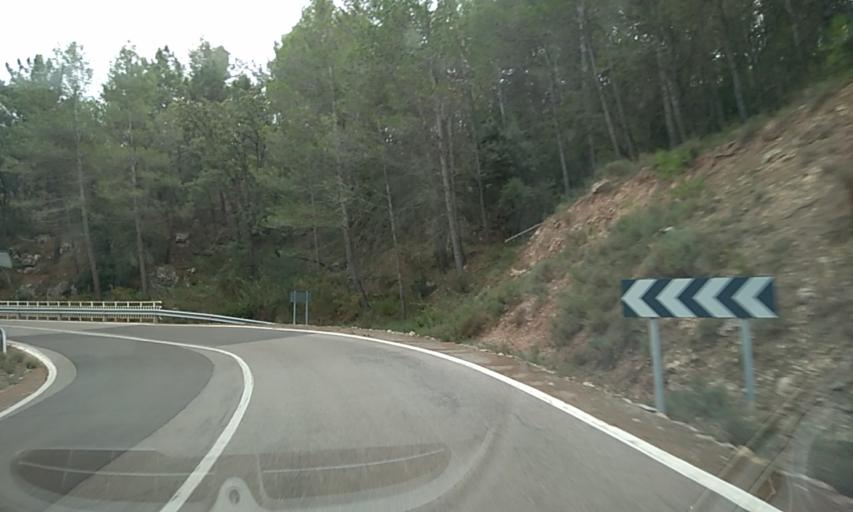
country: ES
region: Valencia
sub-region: Provincia de Castello
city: Puebla de Arenoso
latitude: 40.0922
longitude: -0.5672
